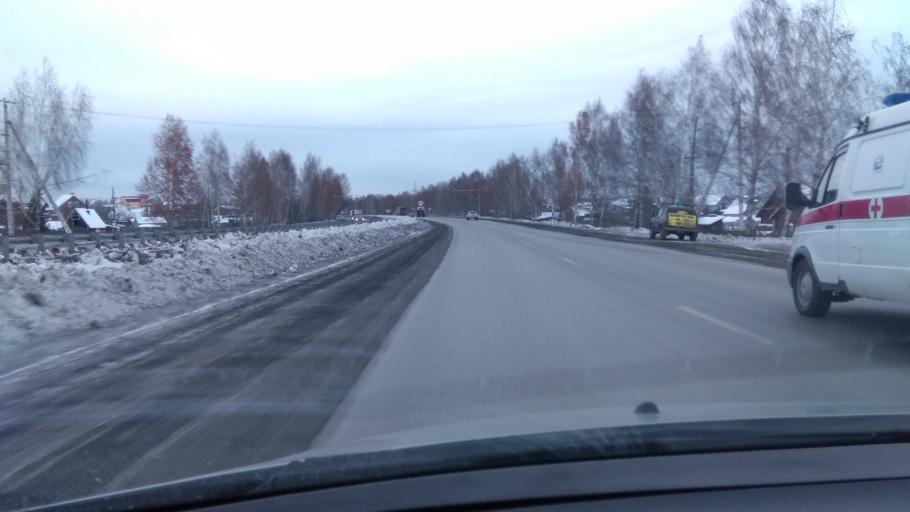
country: RU
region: Sverdlovsk
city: Aramil
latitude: 56.6998
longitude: 60.7497
